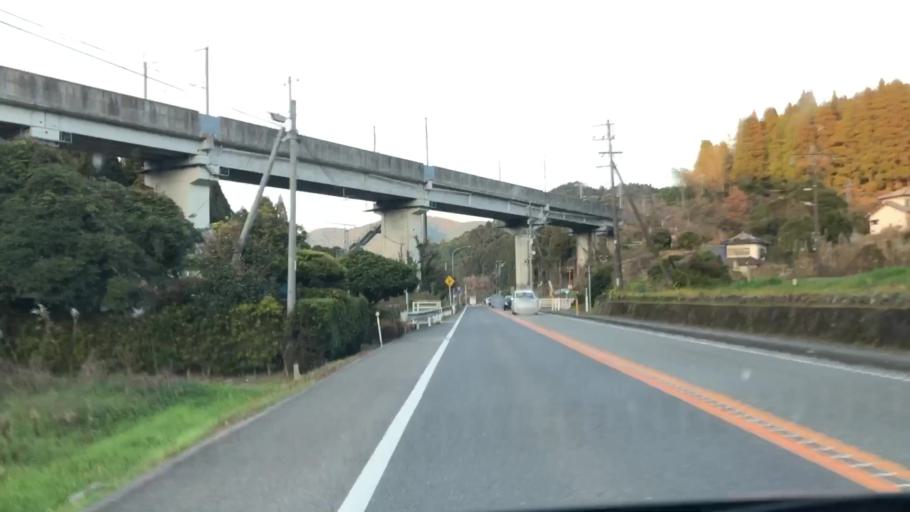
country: JP
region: Kumamoto
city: Minamata
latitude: 32.2167
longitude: 130.4373
